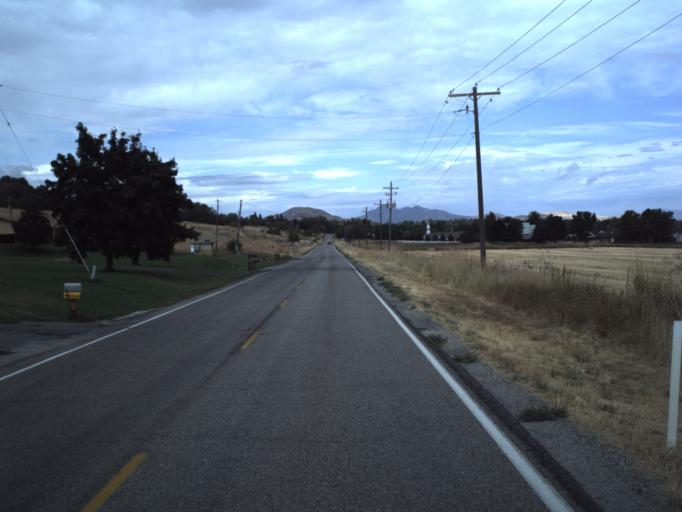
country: US
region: Utah
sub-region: Cache County
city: Mendon
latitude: 41.6914
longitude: -111.9698
